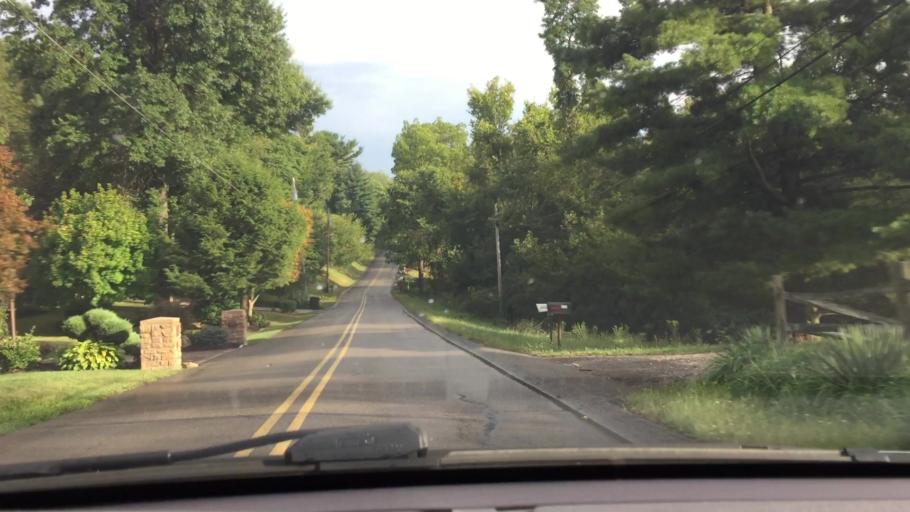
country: US
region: Pennsylvania
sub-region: Washington County
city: McGovern
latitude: 40.2169
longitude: -80.1864
